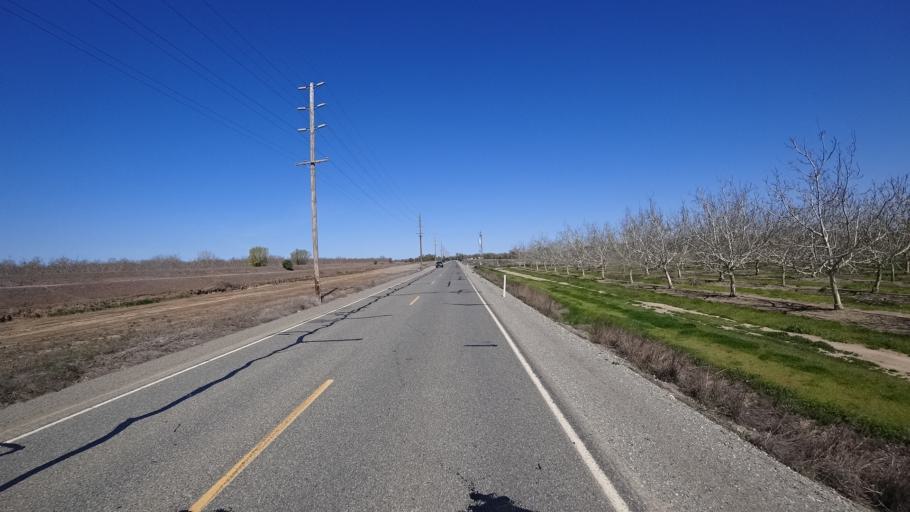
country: US
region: California
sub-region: Glenn County
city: Hamilton City
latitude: 39.7593
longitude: -122.0266
